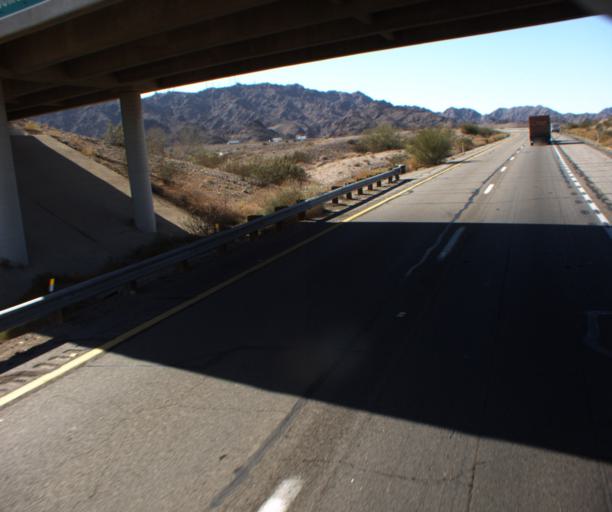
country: US
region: Arizona
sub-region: Yuma County
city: Fortuna Foothills
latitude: 32.6724
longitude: -114.3032
